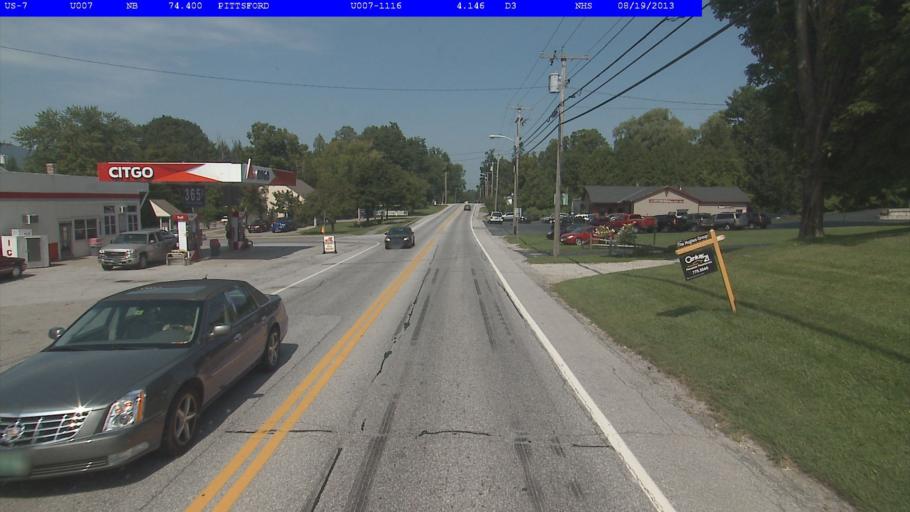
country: US
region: Vermont
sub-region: Rutland County
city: Brandon
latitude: 43.7086
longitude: -73.0301
